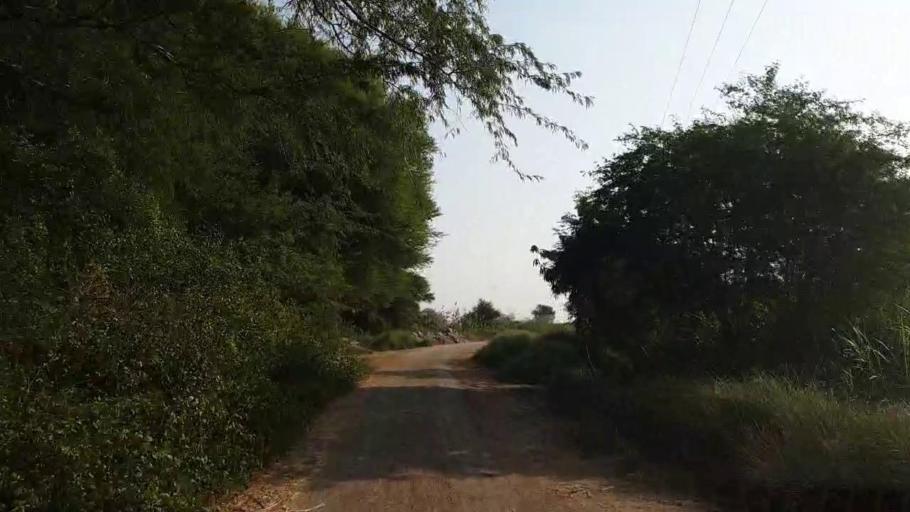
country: PK
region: Sindh
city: Bulri
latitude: 24.9786
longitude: 68.3779
